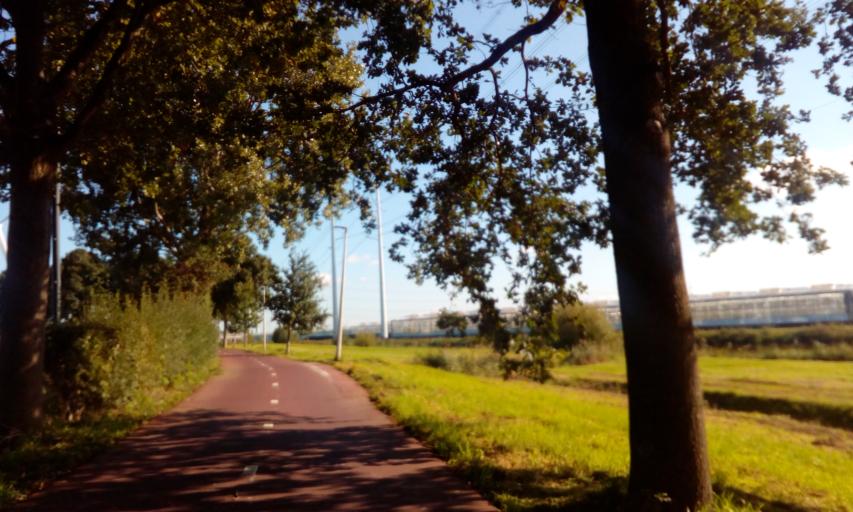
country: NL
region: South Holland
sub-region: Gemeente Zoetermeer
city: Zoetermeer
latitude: 52.0326
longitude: 4.5066
